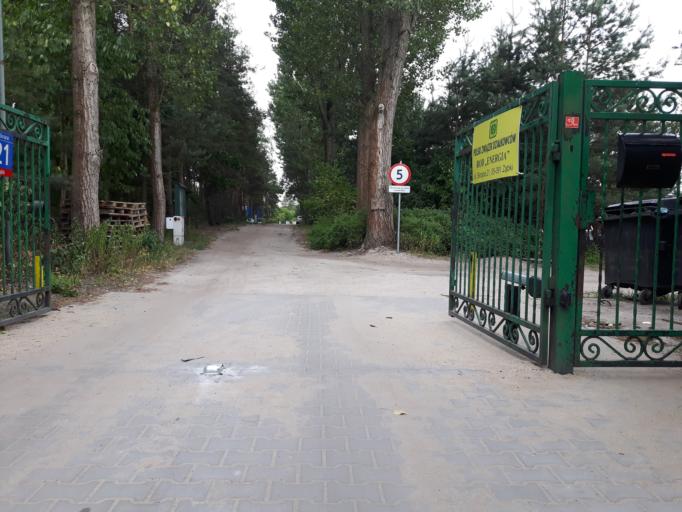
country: PL
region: Masovian Voivodeship
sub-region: Powiat wolominski
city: Zabki
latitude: 52.2771
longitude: 21.1054
